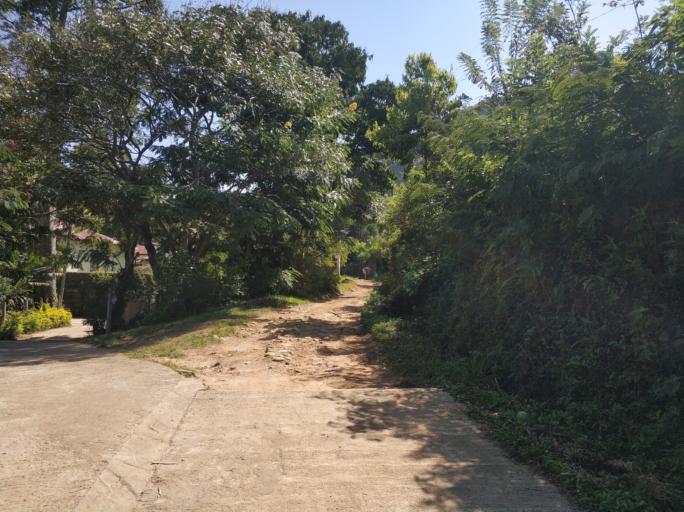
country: LK
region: Uva
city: Haputale
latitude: 6.8323
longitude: 81.0559
